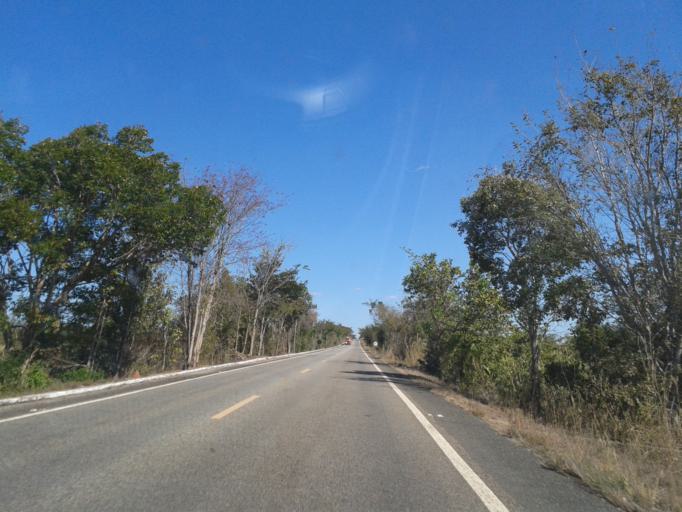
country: BR
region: Goias
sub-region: Sao Miguel Do Araguaia
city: Sao Miguel do Araguaia
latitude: -13.6892
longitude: -50.3311
